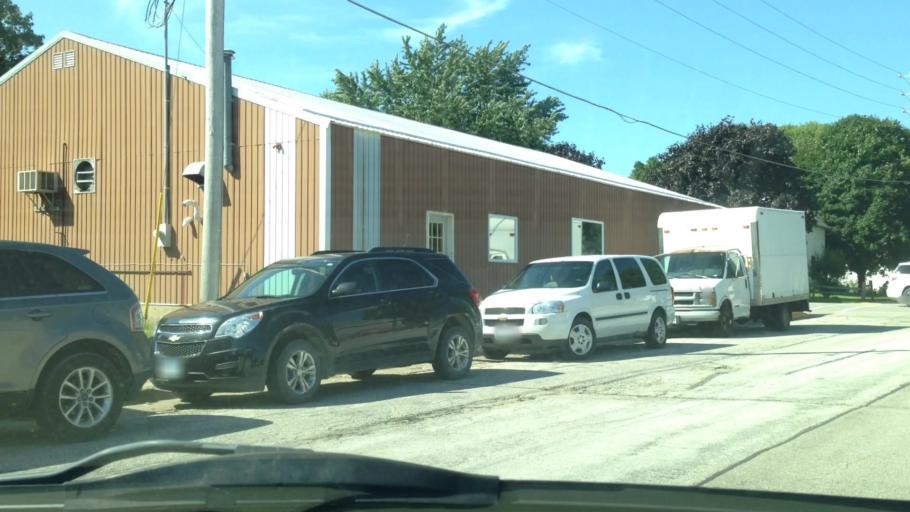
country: US
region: Minnesota
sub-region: Houston County
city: Spring Grove
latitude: 43.5206
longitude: -91.7705
